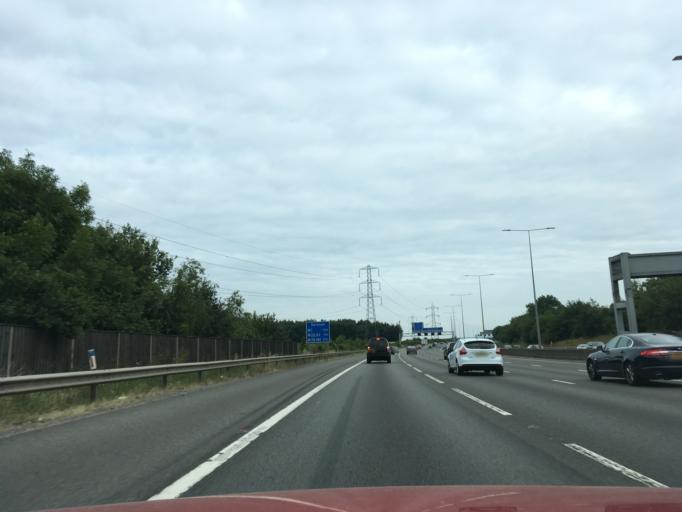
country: GB
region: England
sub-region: Hertfordshire
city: Abbots Langley
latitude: 51.7400
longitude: -0.3958
